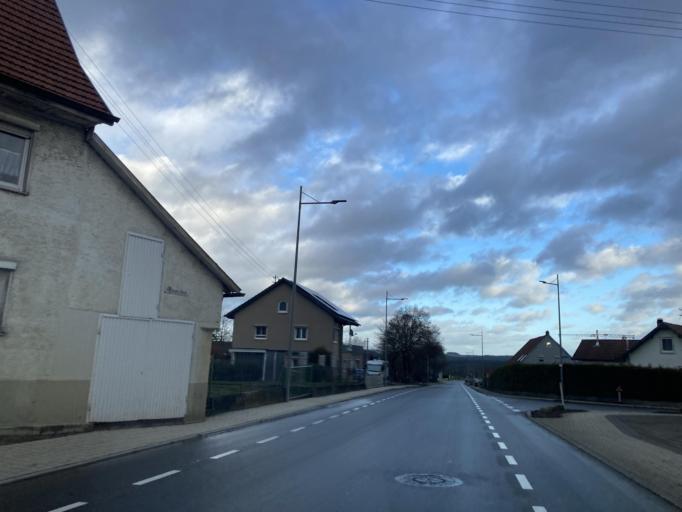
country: DE
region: Baden-Wuerttemberg
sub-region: Freiburg Region
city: Neuhausen ob Eck
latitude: 47.9733
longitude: 8.9317
